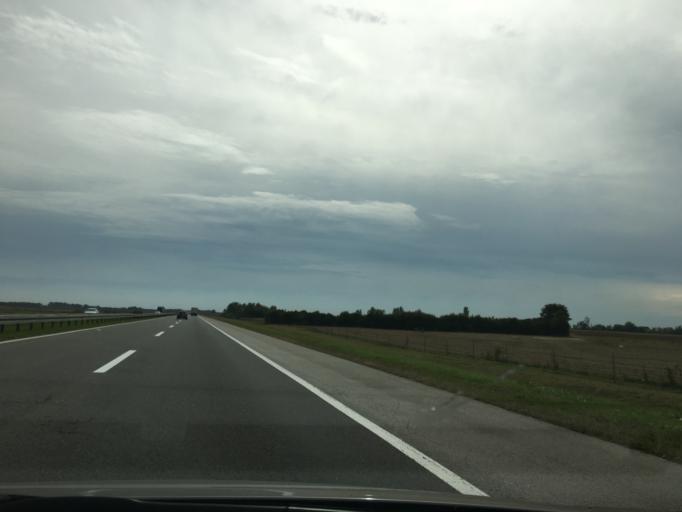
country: RS
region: Autonomna Pokrajina Vojvodina
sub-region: Sremski Okrug
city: Stara Pazova
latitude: 45.0247
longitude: 20.1910
